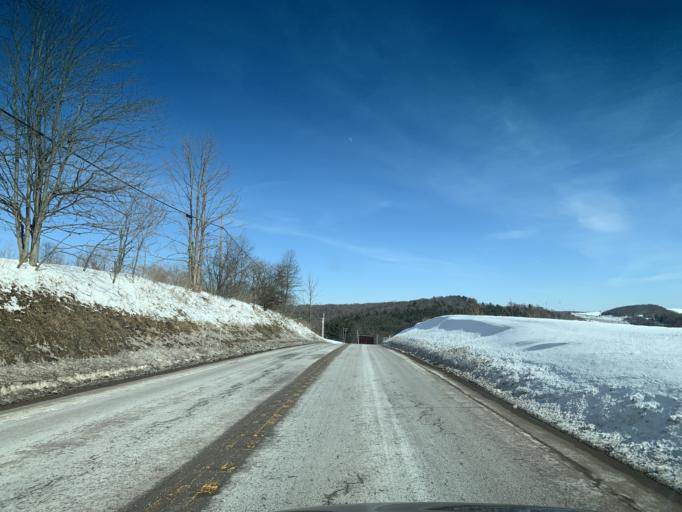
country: US
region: Pennsylvania
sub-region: Somerset County
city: Meyersdale
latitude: 39.6842
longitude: -79.0609
